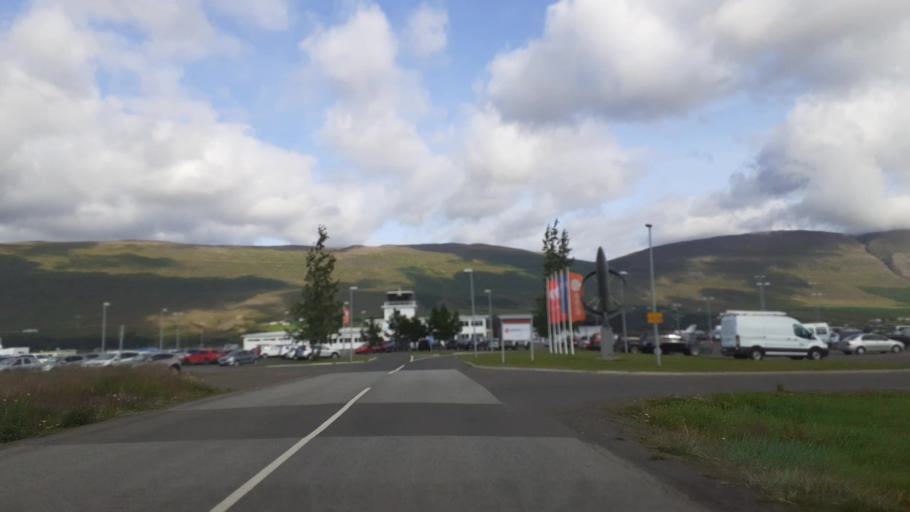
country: IS
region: Northeast
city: Akureyri
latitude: 65.6545
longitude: -18.0791
